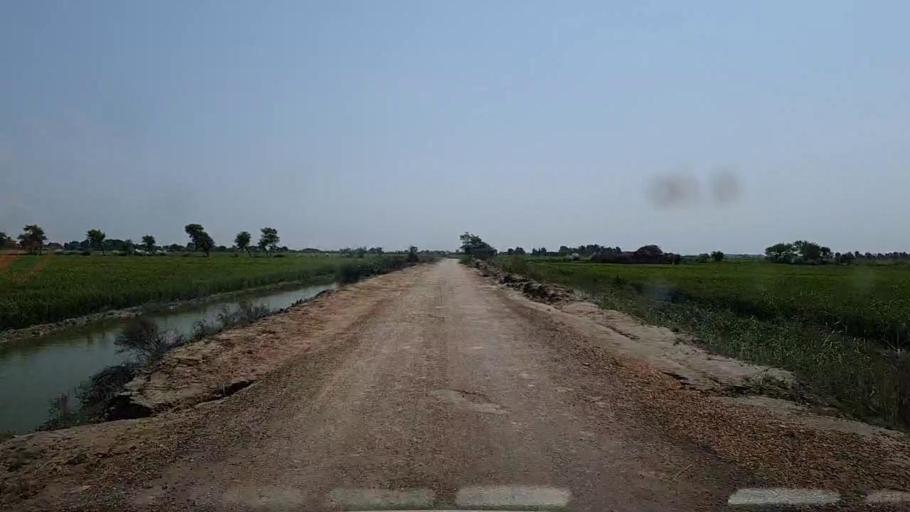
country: PK
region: Sindh
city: Mirpur Batoro
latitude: 24.6067
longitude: 68.4523
